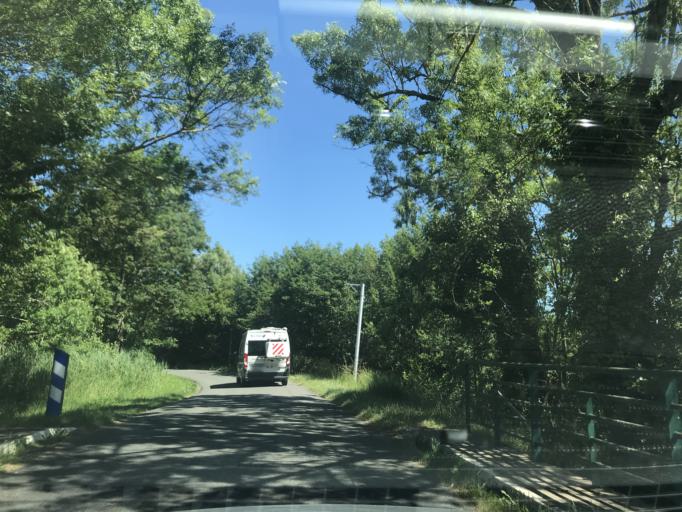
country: FR
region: Poitou-Charentes
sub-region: Departement de la Charente-Maritime
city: Mortagne-sur-Gironde
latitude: 45.4247
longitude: -0.7437
